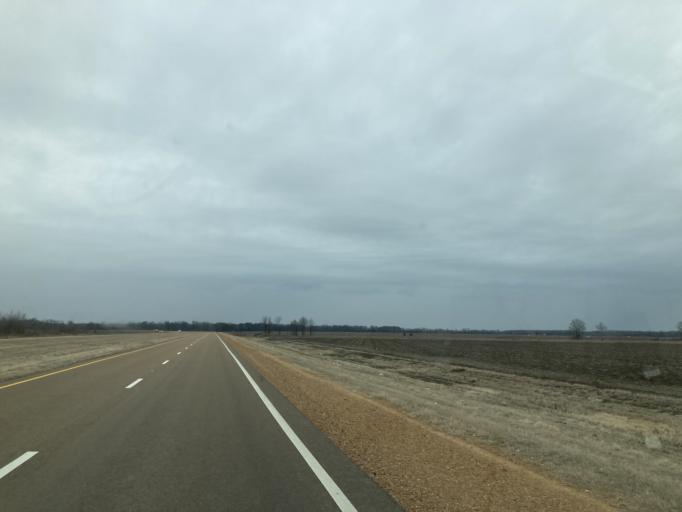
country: US
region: Mississippi
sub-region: Humphreys County
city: Belzoni
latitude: 33.0643
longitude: -90.4719
